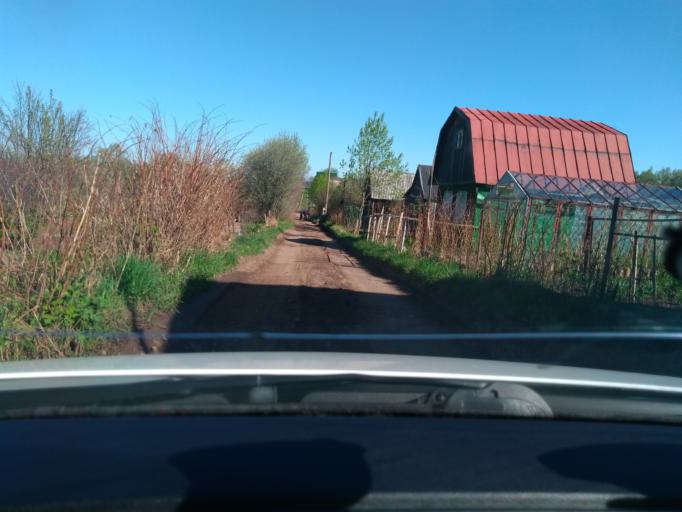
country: RU
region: Perm
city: Lobanovo
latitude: 57.8673
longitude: 56.3054
